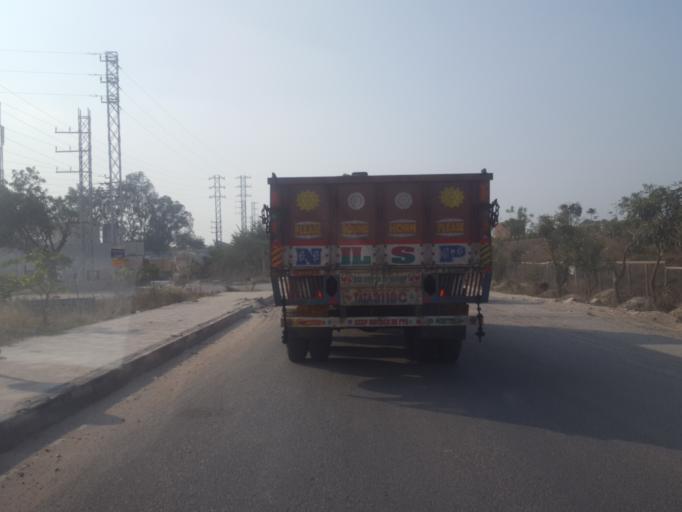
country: IN
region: Telangana
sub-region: Medak
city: Serilingampalle
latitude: 17.4112
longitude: 78.3155
